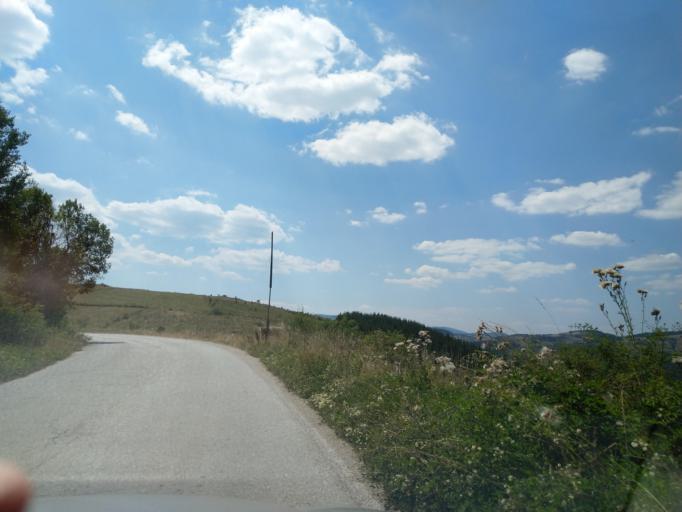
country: RS
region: Central Serbia
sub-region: Zlatiborski Okrug
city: Nova Varos
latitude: 43.4346
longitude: 19.9509
